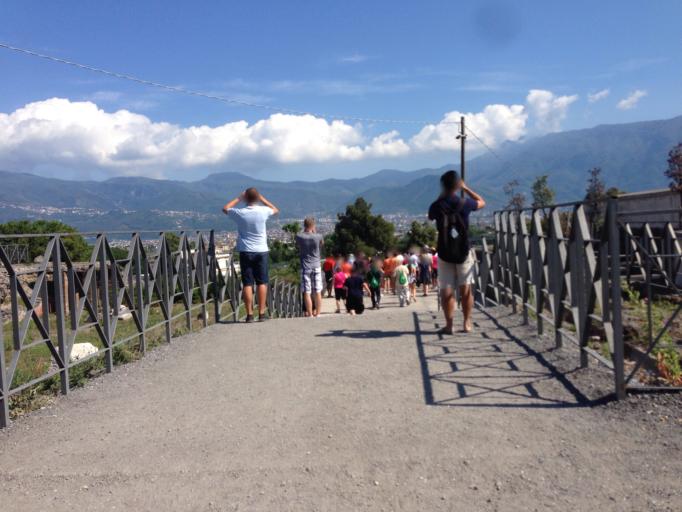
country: IT
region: Campania
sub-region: Provincia di Napoli
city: Pompei
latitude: 40.7485
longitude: 14.4835
